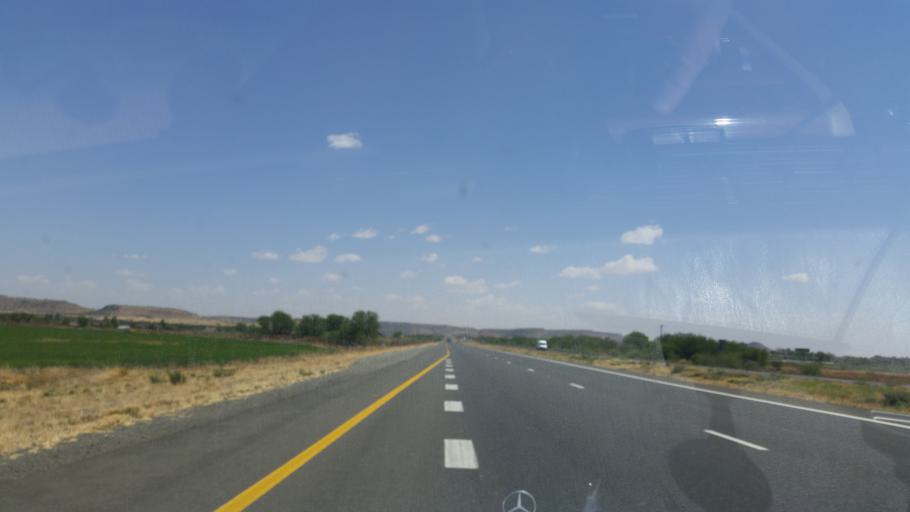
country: ZA
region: Orange Free State
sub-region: Mangaung Metropolitan Municipality
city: Bloemfontein
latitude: -28.9667
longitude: 26.3413
